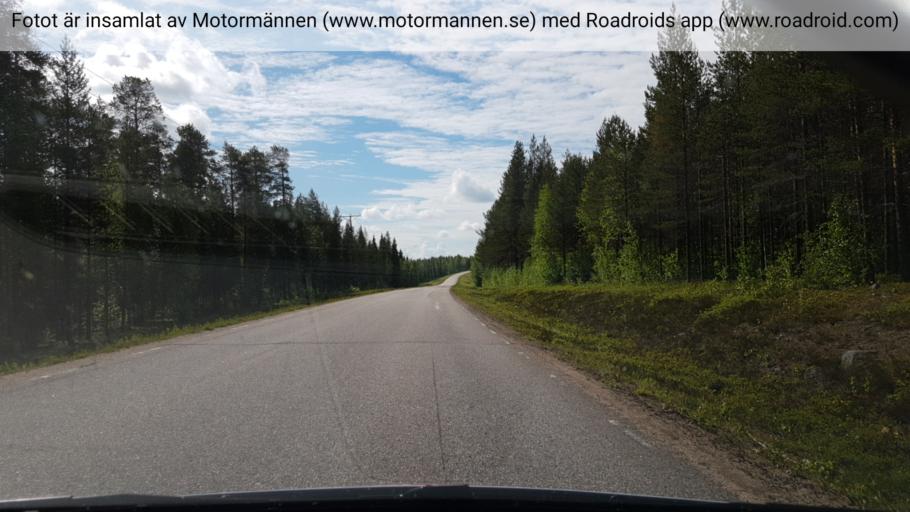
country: FI
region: Lapland
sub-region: Torniolaakso
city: Pello
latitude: 66.6181
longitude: 23.8651
